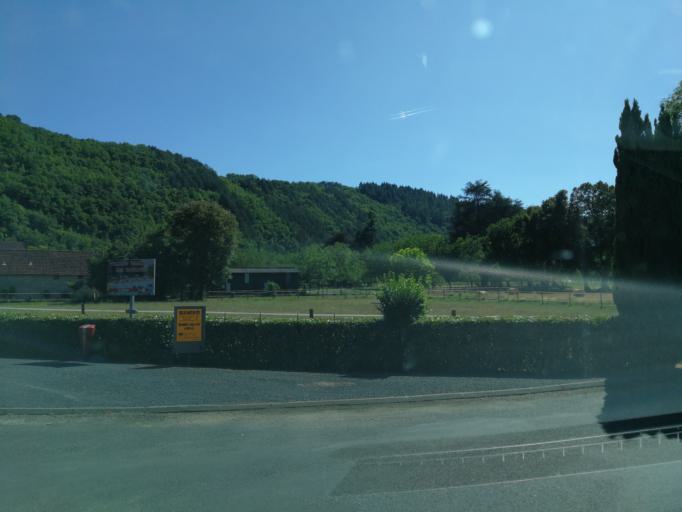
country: FR
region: Midi-Pyrenees
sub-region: Departement du Lot
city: Souillac
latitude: 44.8678
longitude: 1.4410
